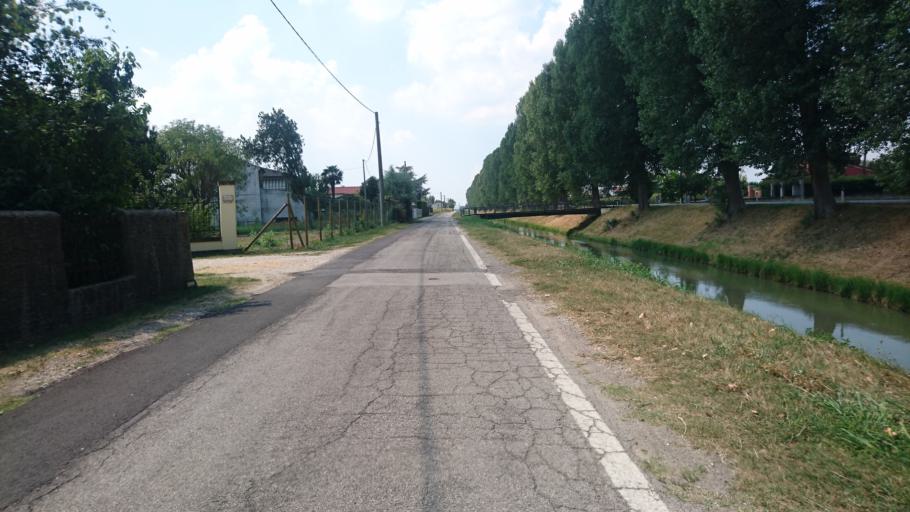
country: IT
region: Veneto
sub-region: Provincia di Padova
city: Sant'Angelo di Piove di Sacco
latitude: 45.3042
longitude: 12.0075
